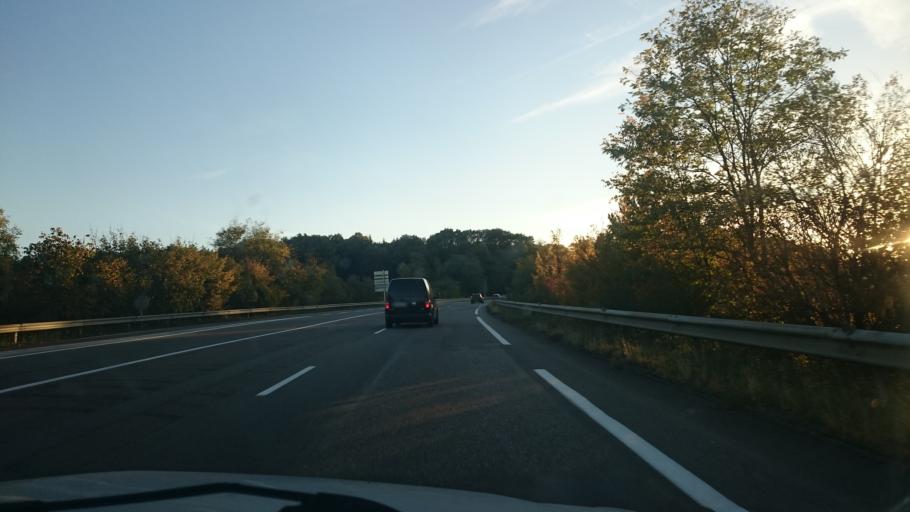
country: FR
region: Franche-Comte
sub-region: Departement du Jura
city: Mouchard
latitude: 46.9781
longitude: 5.8099
